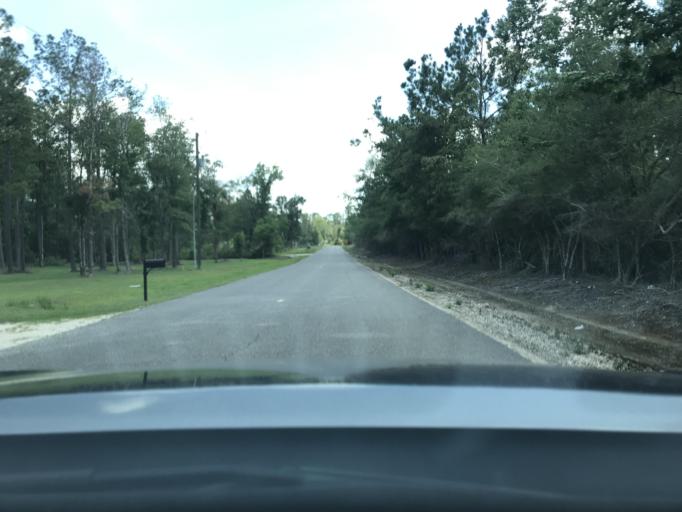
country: US
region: Louisiana
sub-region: Calcasieu Parish
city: Moss Bluff
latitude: 30.3328
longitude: -93.1308
